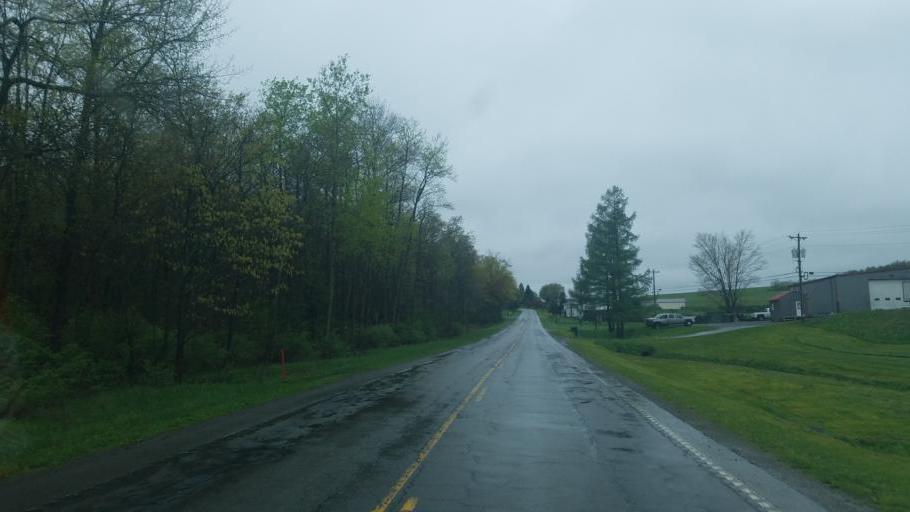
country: US
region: Pennsylvania
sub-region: Potter County
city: Coudersport
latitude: 41.8789
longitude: -77.8184
